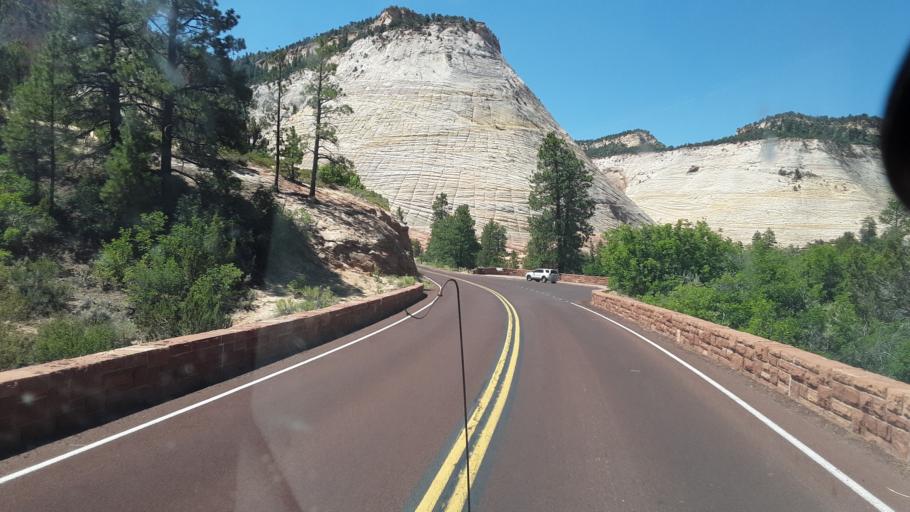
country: US
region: Utah
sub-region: Washington County
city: Hildale
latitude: 37.2309
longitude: -112.8777
